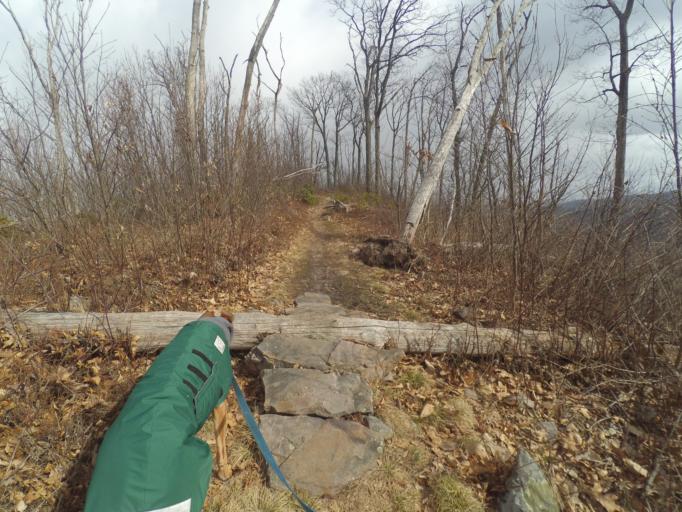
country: US
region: Pennsylvania
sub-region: Centre County
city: Boalsburg
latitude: 40.7526
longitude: -77.7302
